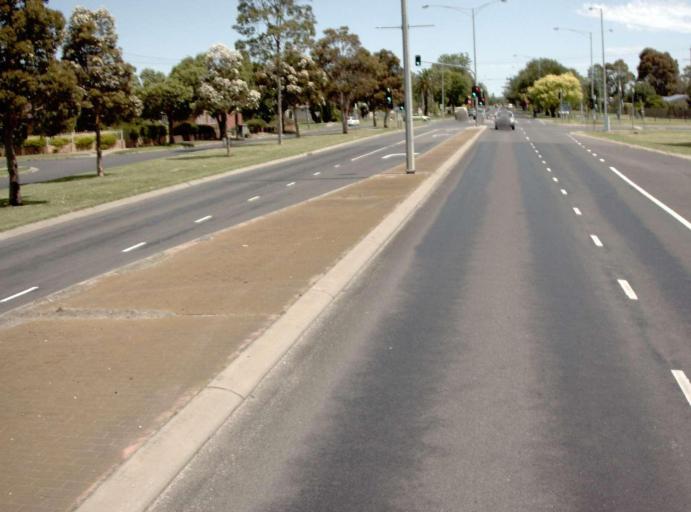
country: AU
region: Victoria
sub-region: Wellington
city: Sale
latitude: -38.0923
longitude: 147.0691
